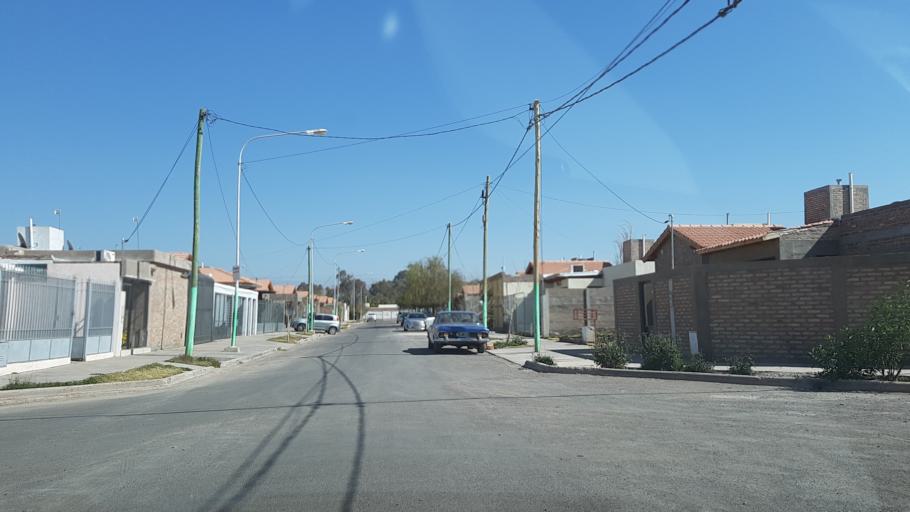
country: AR
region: San Juan
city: San Juan
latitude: -31.5224
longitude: -68.5908
